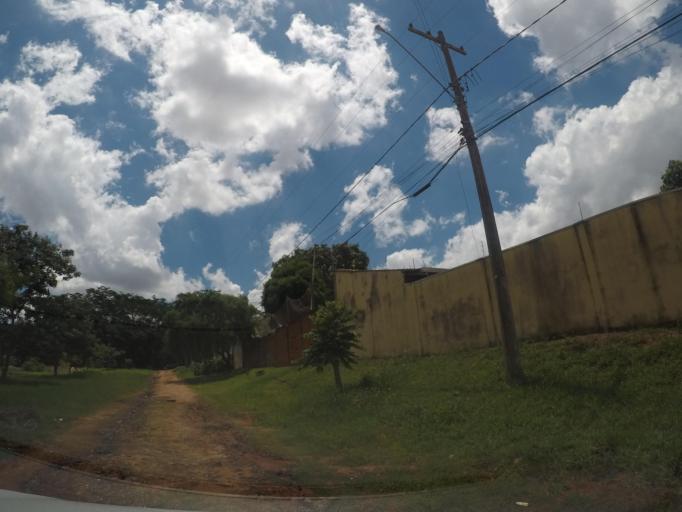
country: BR
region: Sao Paulo
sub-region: Hortolandia
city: Hortolandia
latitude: -22.8426
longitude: -47.2326
